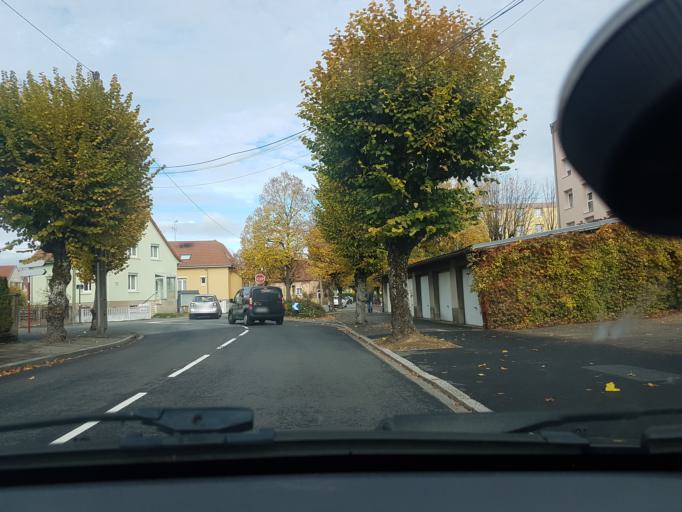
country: FR
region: Franche-Comte
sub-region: Territoire de Belfort
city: Danjoutin
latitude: 47.6244
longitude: 6.8522
